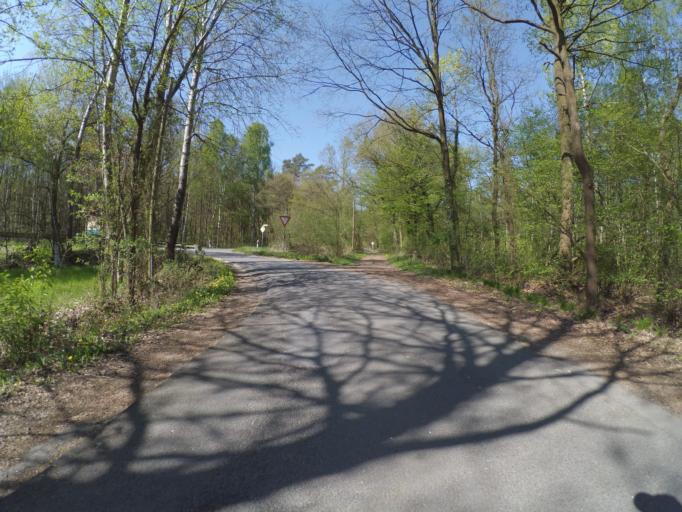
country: DE
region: North Rhine-Westphalia
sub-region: Regierungsbezirk Munster
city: Ascheberg
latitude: 51.8416
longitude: 7.5938
